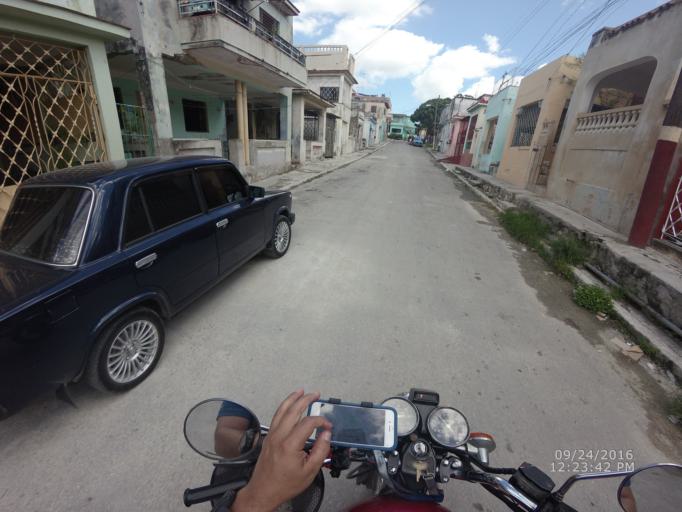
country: CU
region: La Habana
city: Diez de Octubre
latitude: 23.0995
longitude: -82.3525
